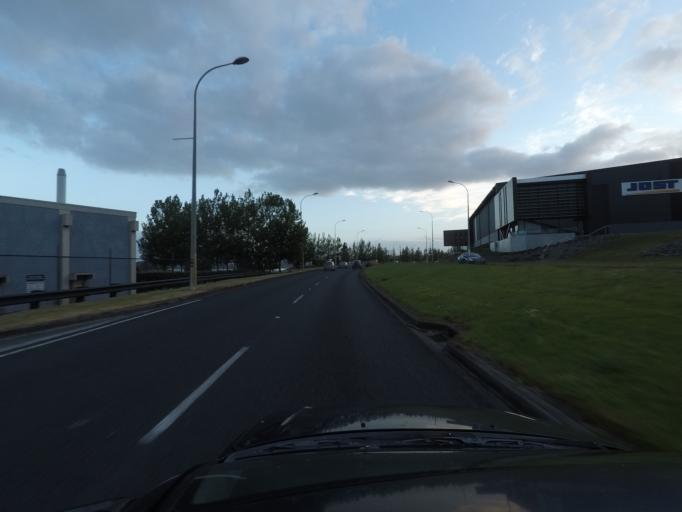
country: NZ
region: Auckland
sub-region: Auckland
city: Tamaki
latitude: -36.9410
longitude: 174.8636
